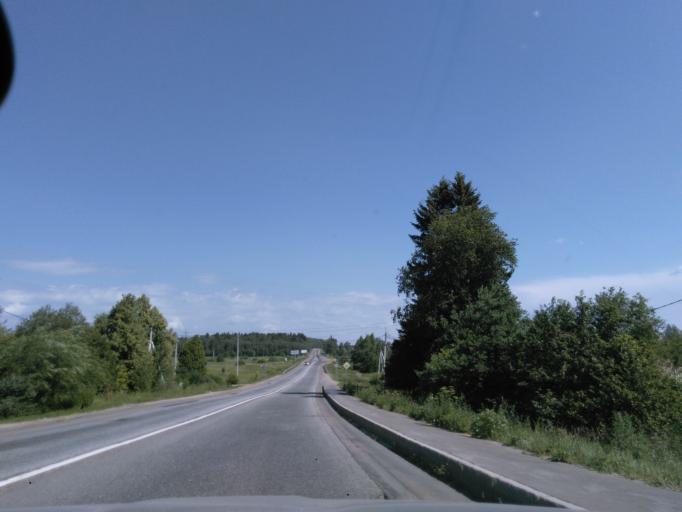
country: RU
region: Moskovskaya
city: Solnechnogorsk
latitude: 56.1505
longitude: 36.9184
